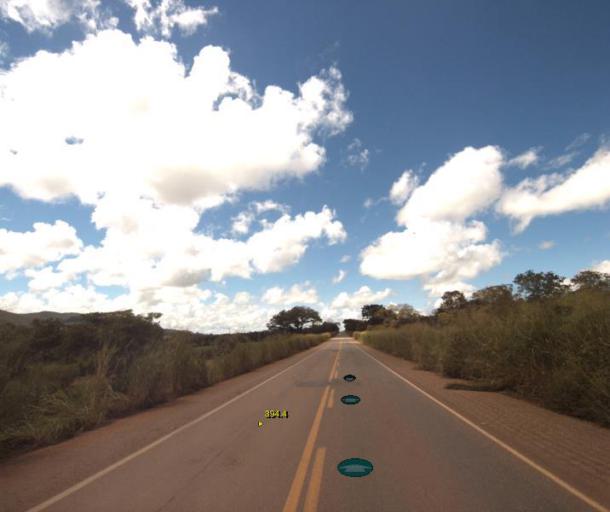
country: BR
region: Goias
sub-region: Petrolina De Goias
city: Petrolina de Goias
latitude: -15.9961
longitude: -49.1464
